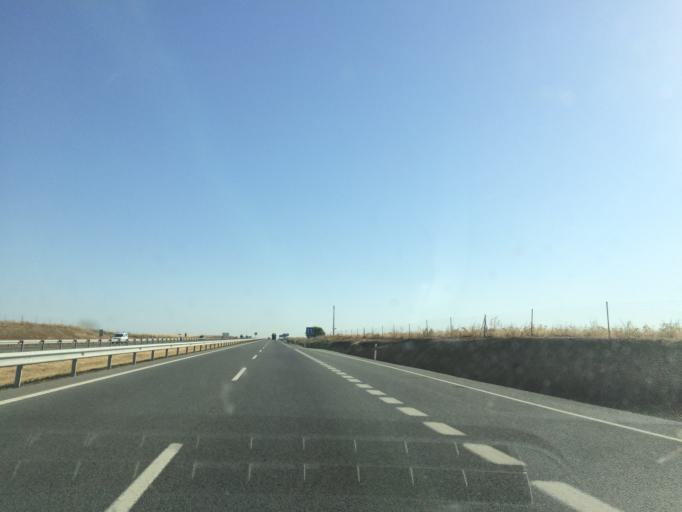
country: ES
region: Castille-La Mancha
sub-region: Province of Toledo
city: Maqueda
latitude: 40.0734
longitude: -4.3619
